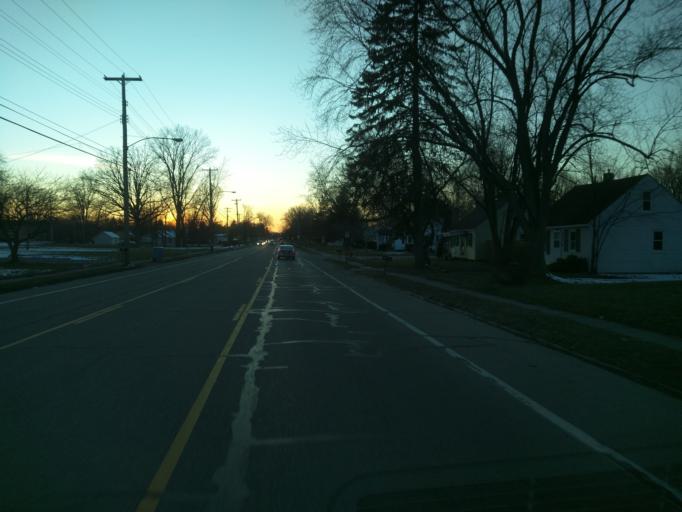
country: US
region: Michigan
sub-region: Ingham County
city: Lansing
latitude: 42.6976
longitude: -84.5848
